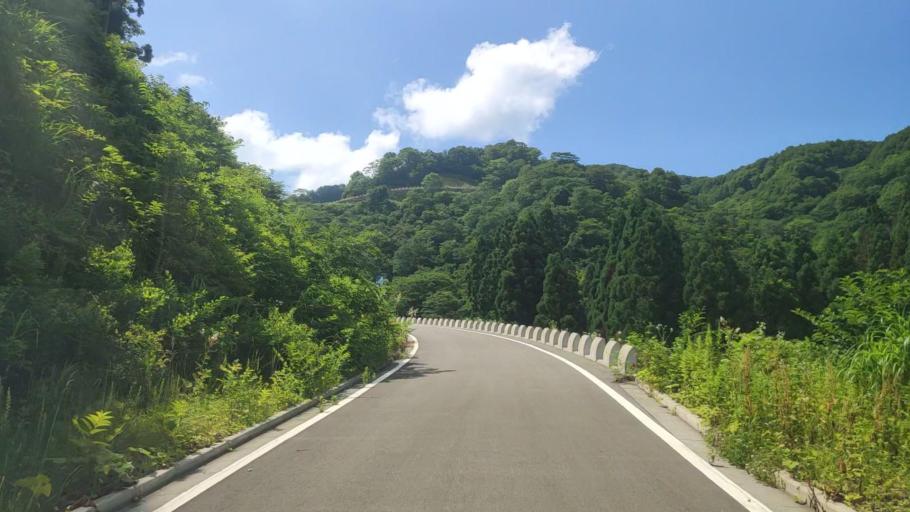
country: JP
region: Fukui
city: Katsuyama
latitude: 36.1557
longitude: 136.5272
